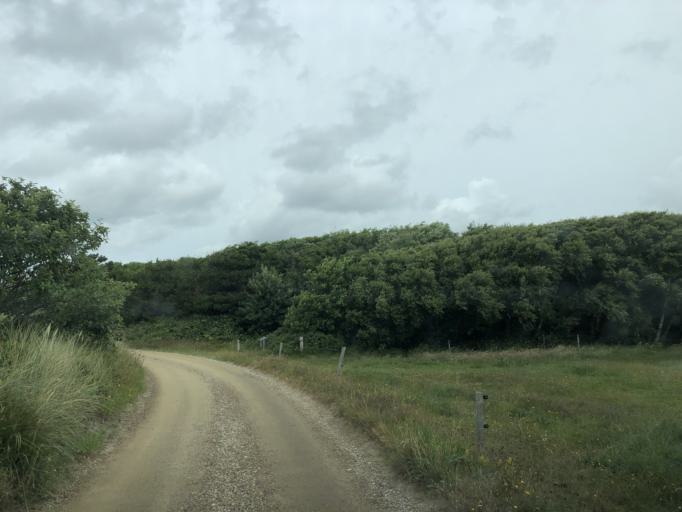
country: DK
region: Central Jutland
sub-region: Ringkobing-Skjern Kommune
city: Hvide Sande
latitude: 55.9229
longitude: 8.1703
